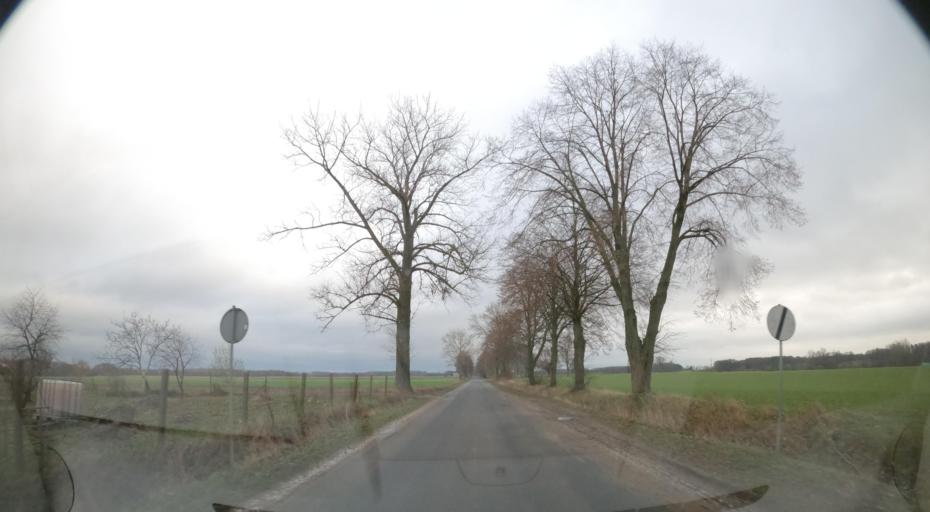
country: PL
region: Greater Poland Voivodeship
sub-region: Powiat pilski
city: Lobzenica
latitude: 53.2578
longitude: 17.1563
